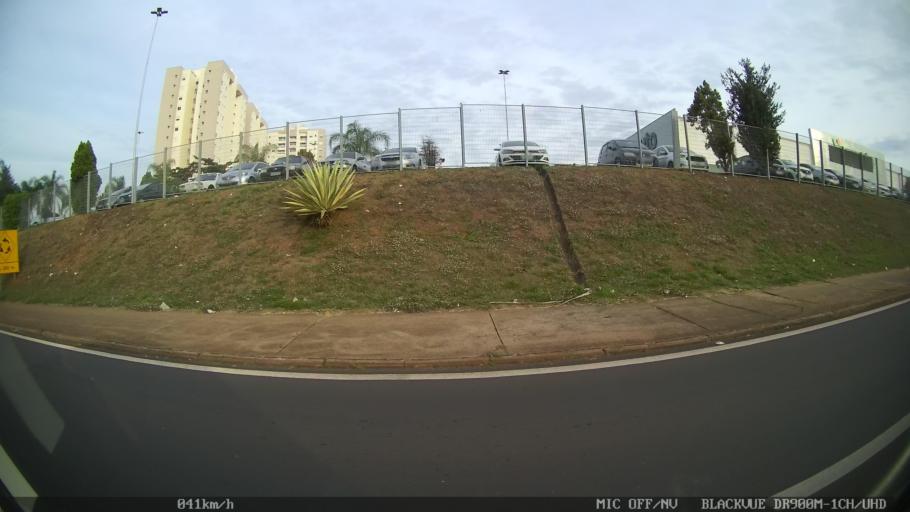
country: BR
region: Sao Paulo
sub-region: Limeira
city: Limeira
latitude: -22.5626
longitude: -47.4212
